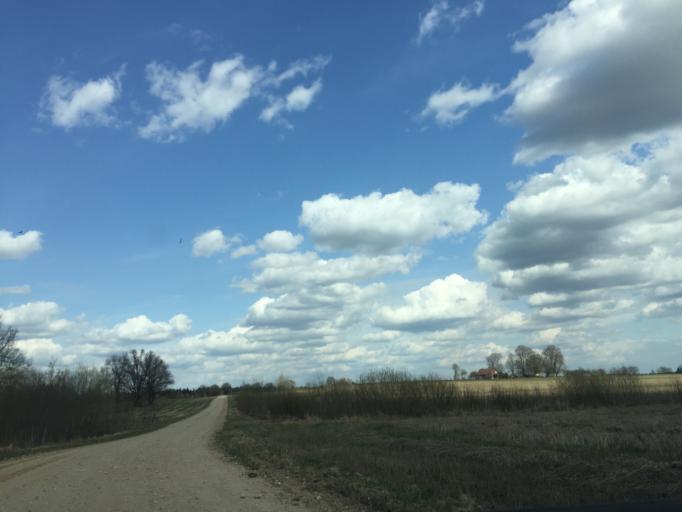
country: LV
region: Skriveri
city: Skriveri
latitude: 56.7567
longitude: 25.1265
